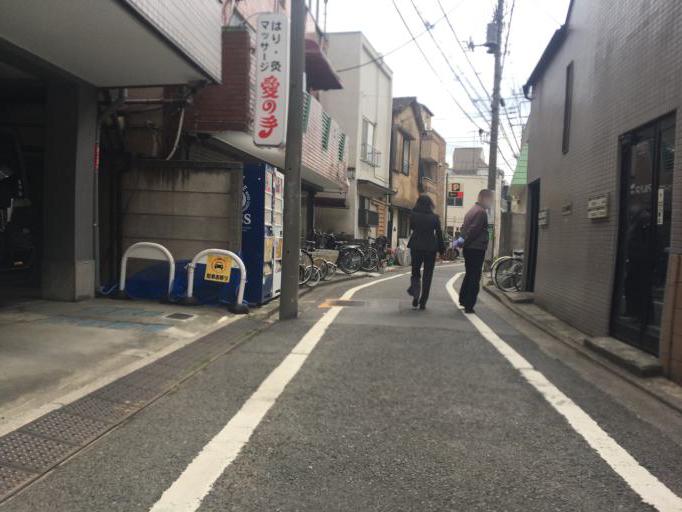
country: JP
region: Tokyo
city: Tokyo
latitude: 35.7044
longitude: 139.6579
